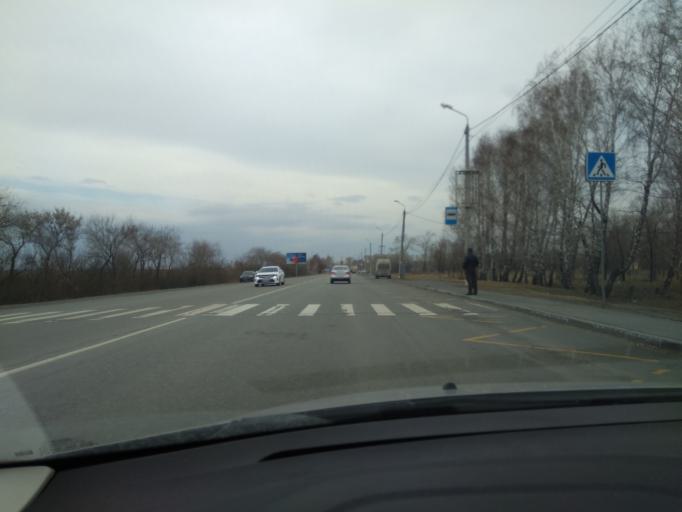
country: RU
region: Chelyabinsk
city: Potanino
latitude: 55.2890
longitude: 61.5105
